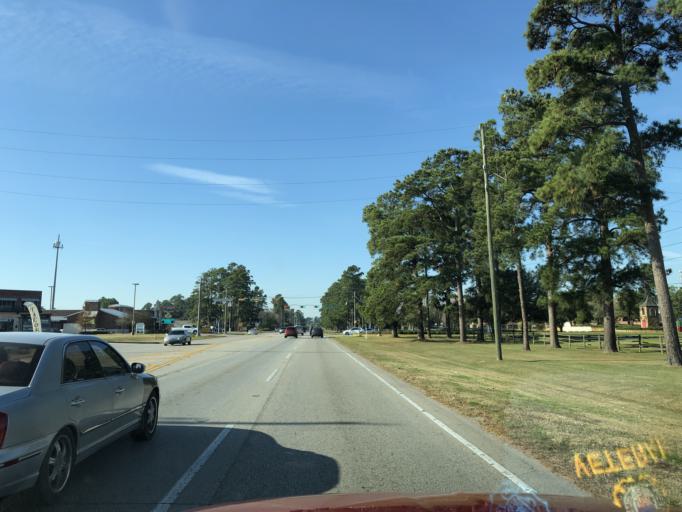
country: US
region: Texas
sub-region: Harris County
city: Tomball
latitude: 30.0277
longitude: -95.5621
